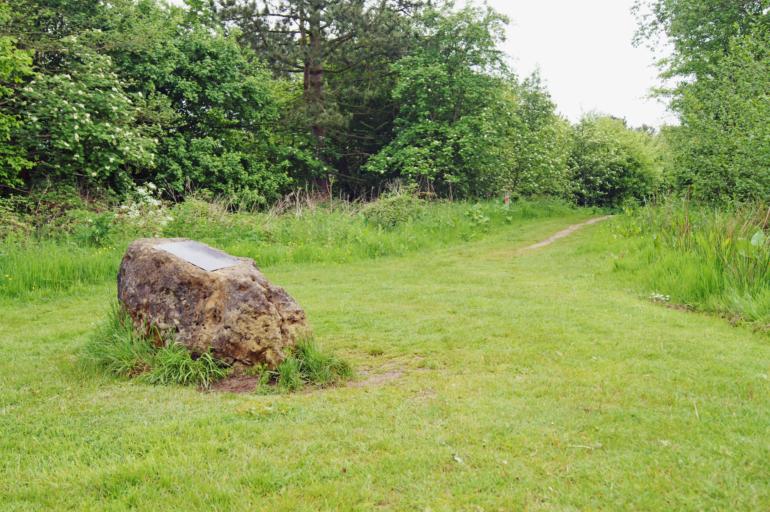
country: GB
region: England
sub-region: Lincolnshire
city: Spilsby
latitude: 53.1986
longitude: -0.0018
